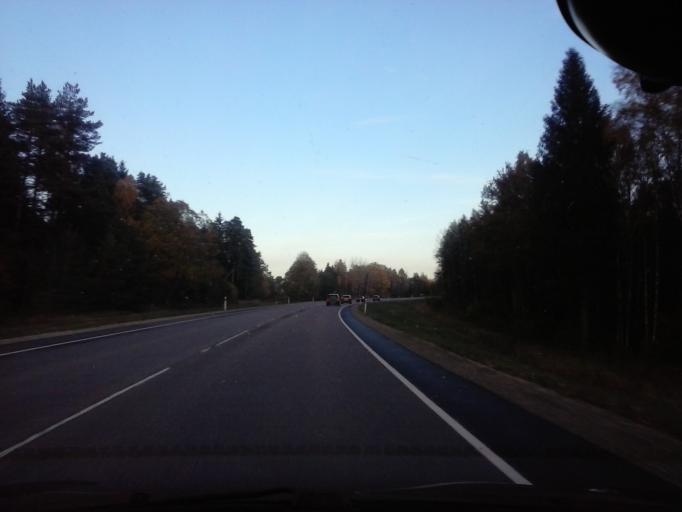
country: EE
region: Harju
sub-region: Nissi vald
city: Turba
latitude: 58.9941
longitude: 24.0374
